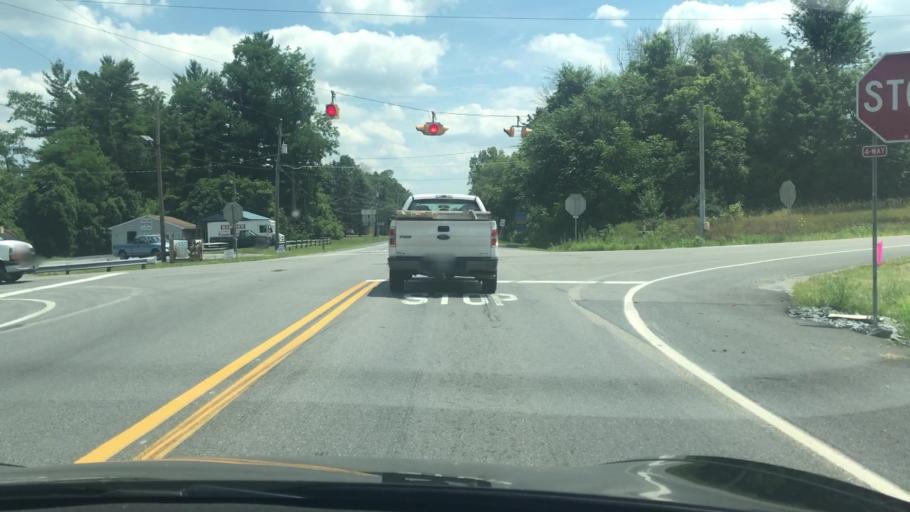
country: US
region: Pennsylvania
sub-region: York County
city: Valley Green
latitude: 40.1323
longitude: -76.8625
